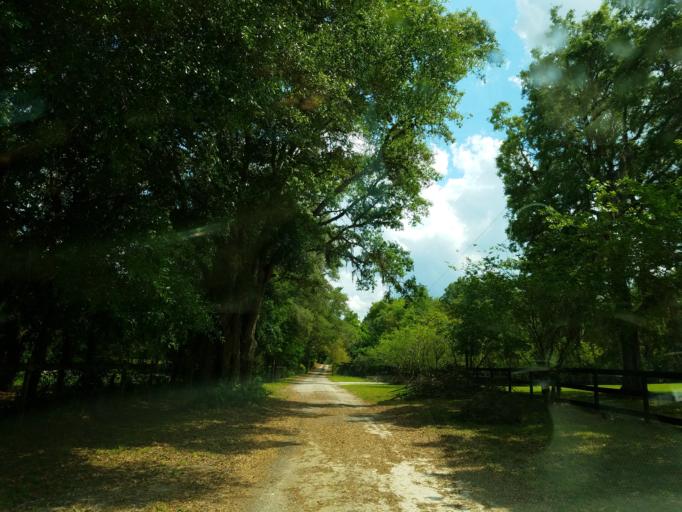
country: US
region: Florida
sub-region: Hernando County
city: Hill 'n Dale
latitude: 28.5329
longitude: -82.2551
